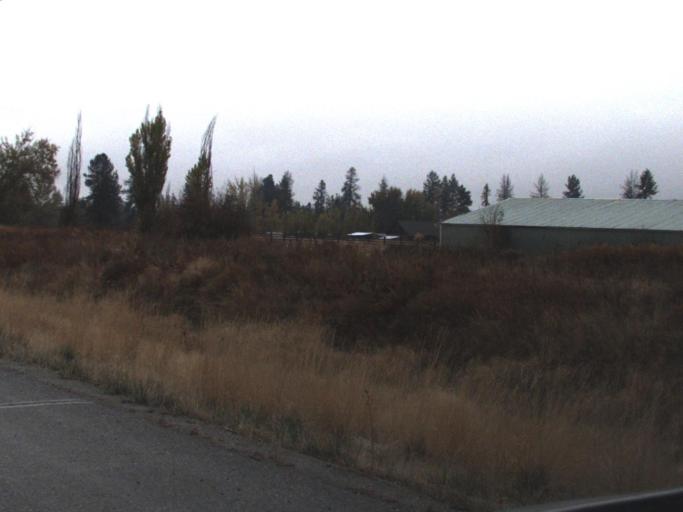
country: US
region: Washington
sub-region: Stevens County
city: Kettle Falls
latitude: 48.6076
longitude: -118.0317
